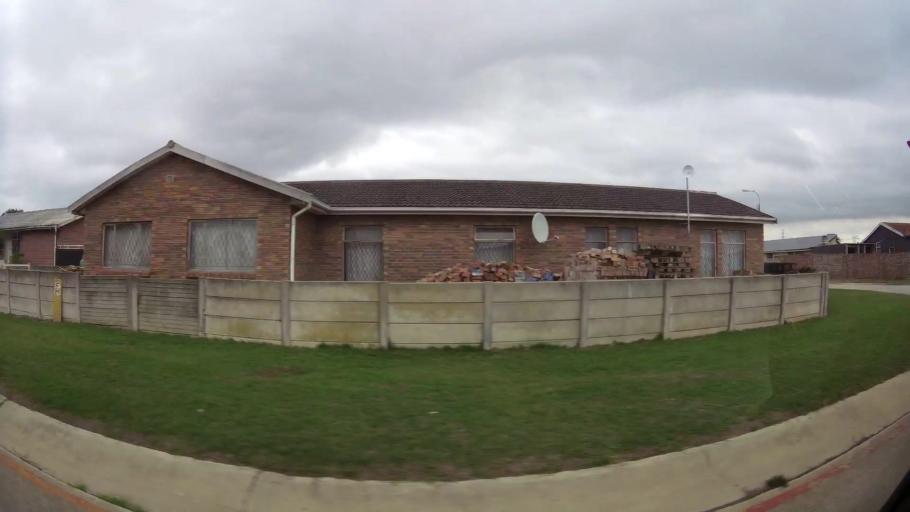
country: ZA
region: Eastern Cape
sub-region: Nelson Mandela Bay Metropolitan Municipality
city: Port Elizabeth
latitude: -33.9175
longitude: 25.5708
